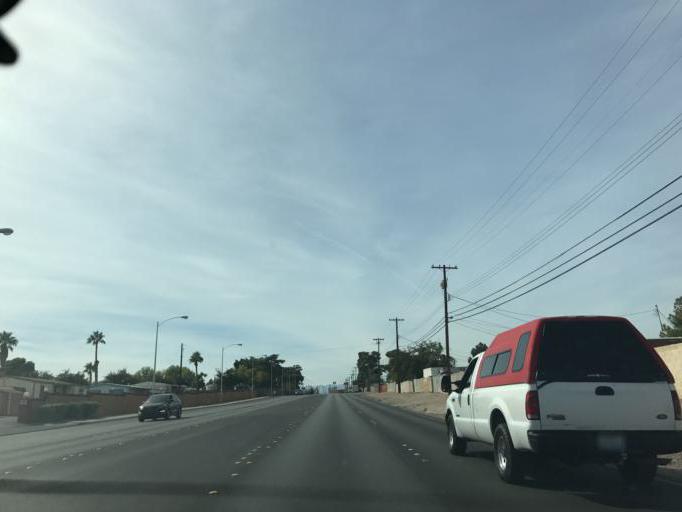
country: US
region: Nevada
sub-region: Clark County
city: Winchester
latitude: 36.1296
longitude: -115.0756
